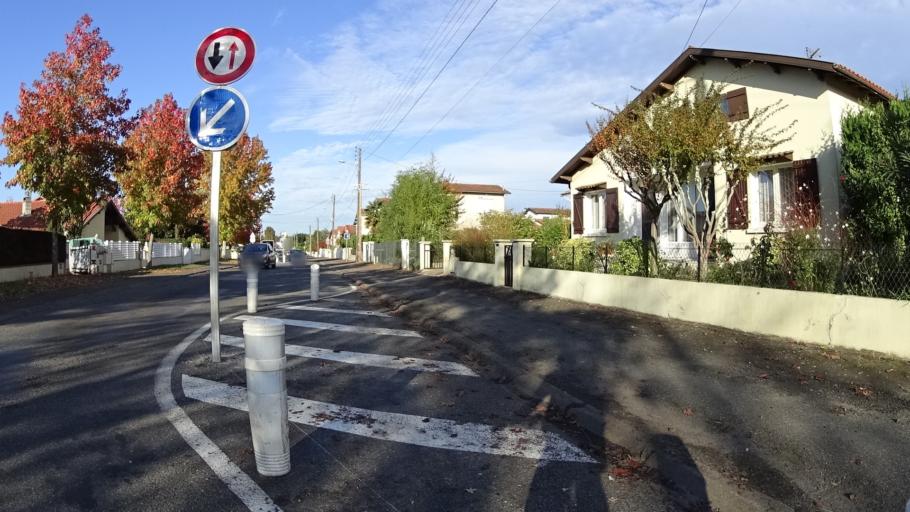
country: FR
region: Aquitaine
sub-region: Departement des Landes
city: Saint-Paul-les-Dax
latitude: 43.7323
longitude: -1.0559
